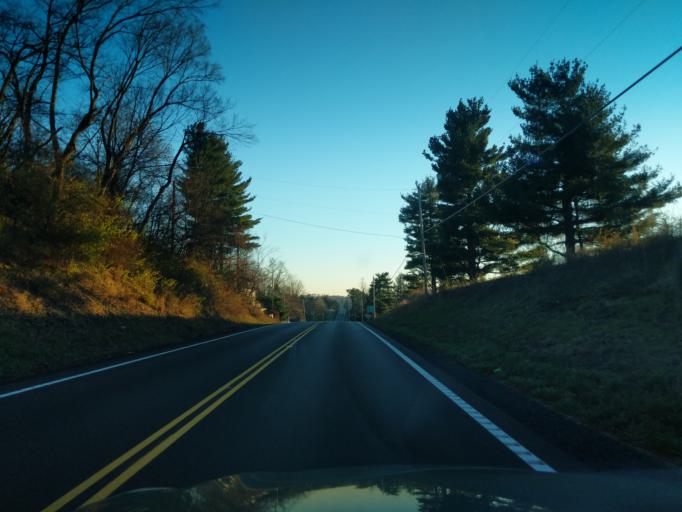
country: US
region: Ohio
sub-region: Licking County
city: Harbor Hills
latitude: 39.9744
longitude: -82.4122
